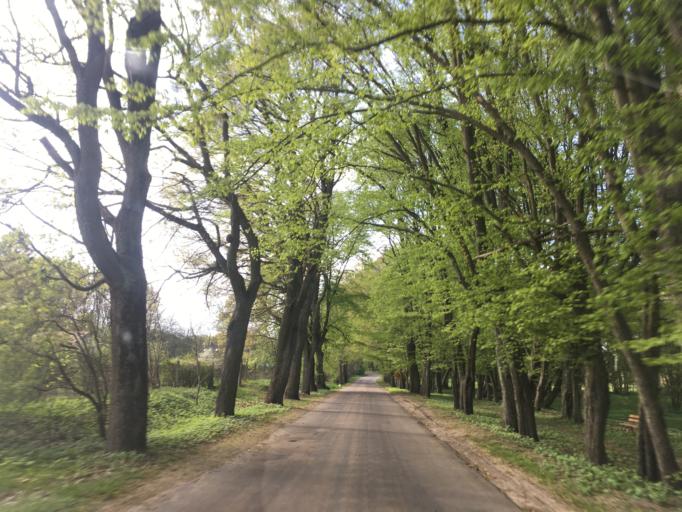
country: PL
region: Warmian-Masurian Voivodeship
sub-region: Powiat nidzicki
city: Nidzica
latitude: 53.4479
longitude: 20.4515
